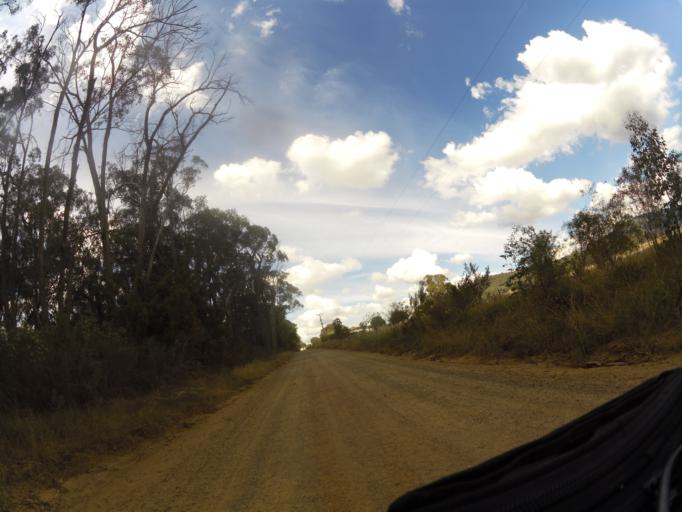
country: AU
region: Victoria
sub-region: Benalla
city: Benalla
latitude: -36.7792
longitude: 145.9769
